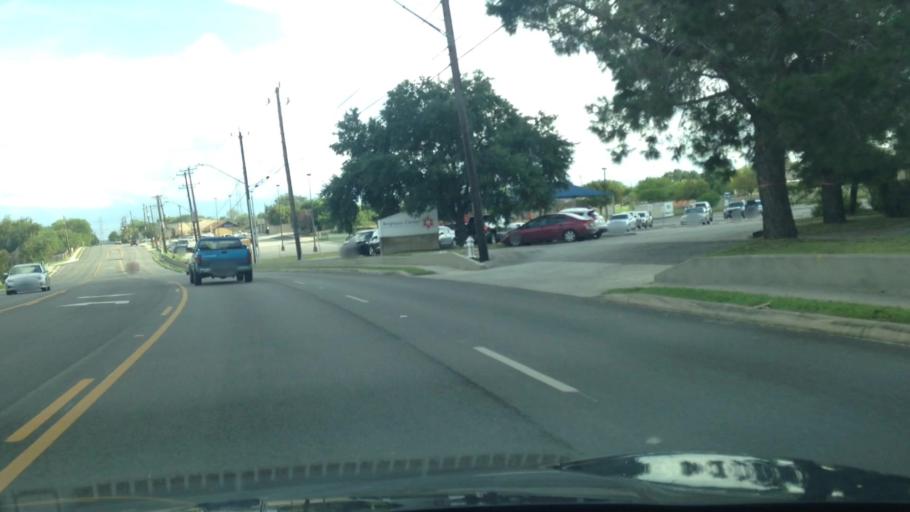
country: US
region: Texas
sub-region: Bexar County
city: Windcrest
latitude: 29.5705
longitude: -98.3960
